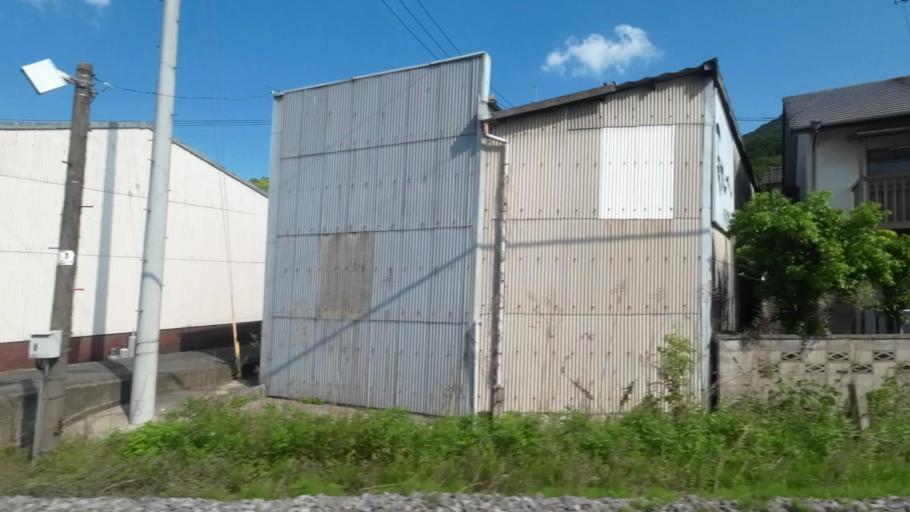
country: JP
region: Kagawa
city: Takamatsu-shi
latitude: 34.3098
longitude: 133.9787
